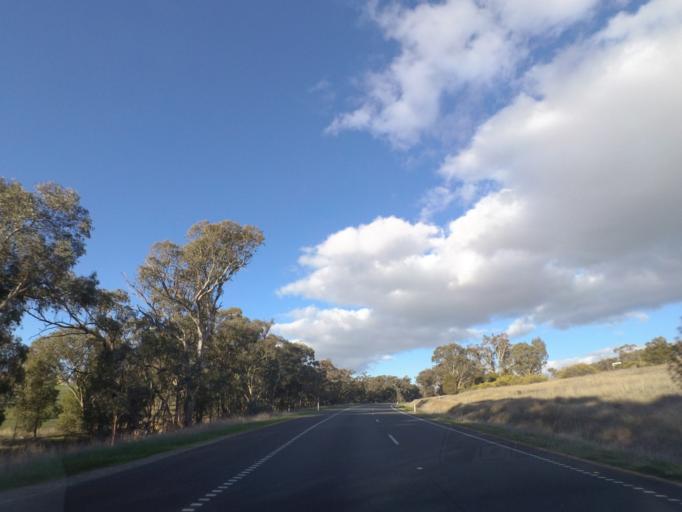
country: AU
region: New South Wales
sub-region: Gundagai
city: Gundagai
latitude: -34.8115
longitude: 148.4198
